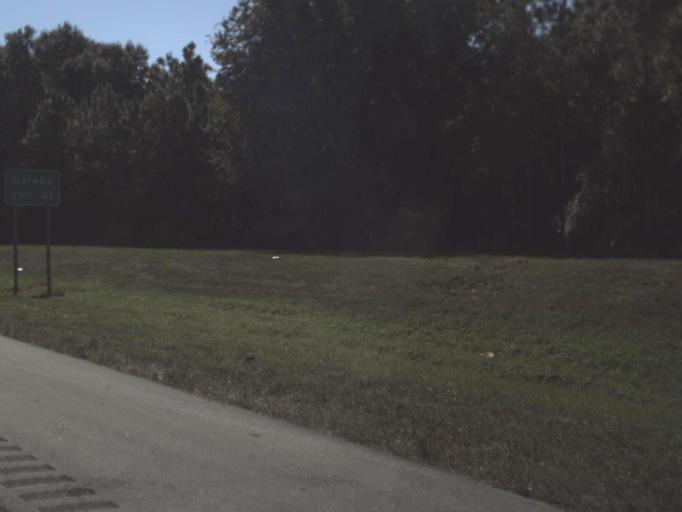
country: US
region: Florida
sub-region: Seminole County
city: Oviedo
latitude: 28.6729
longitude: -81.2266
